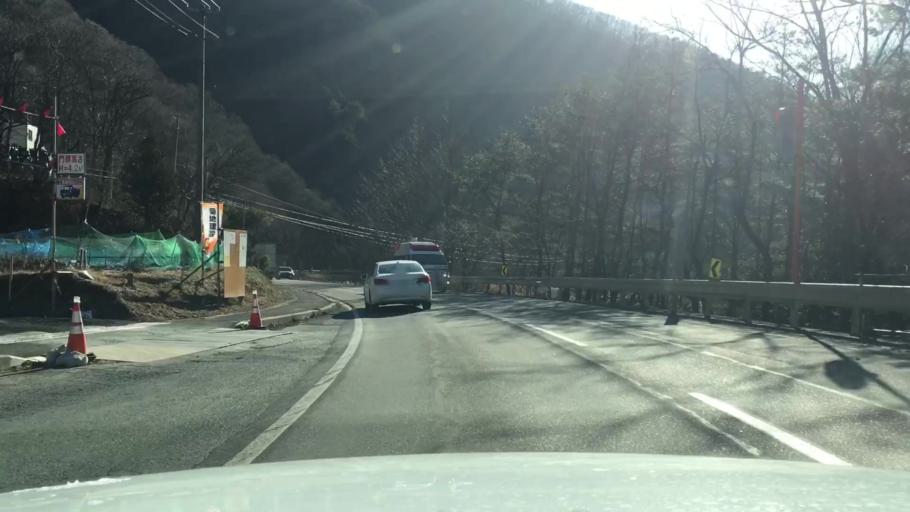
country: JP
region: Iwate
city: Miyako
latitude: 39.6088
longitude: 141.6500
